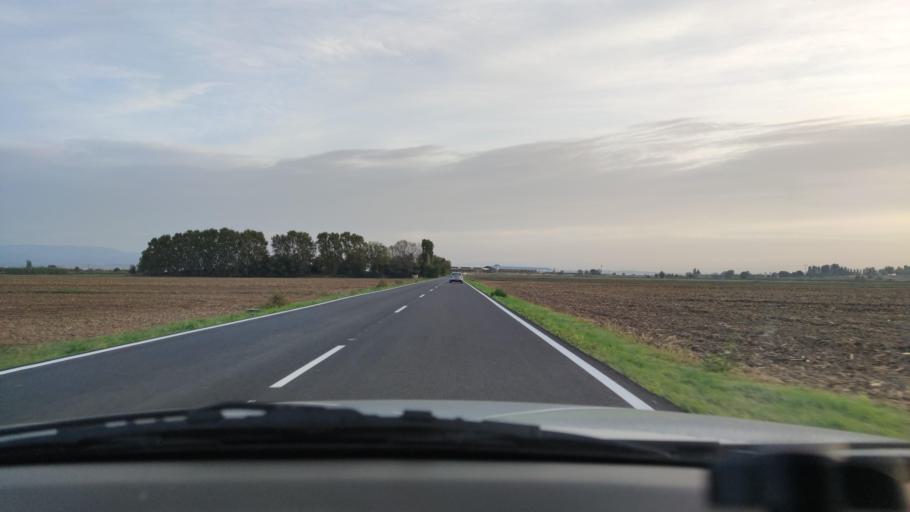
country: ES
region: Catalonia
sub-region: Provincia de Lleida
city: Mollerussa
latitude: 41.6546
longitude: 0.8898
